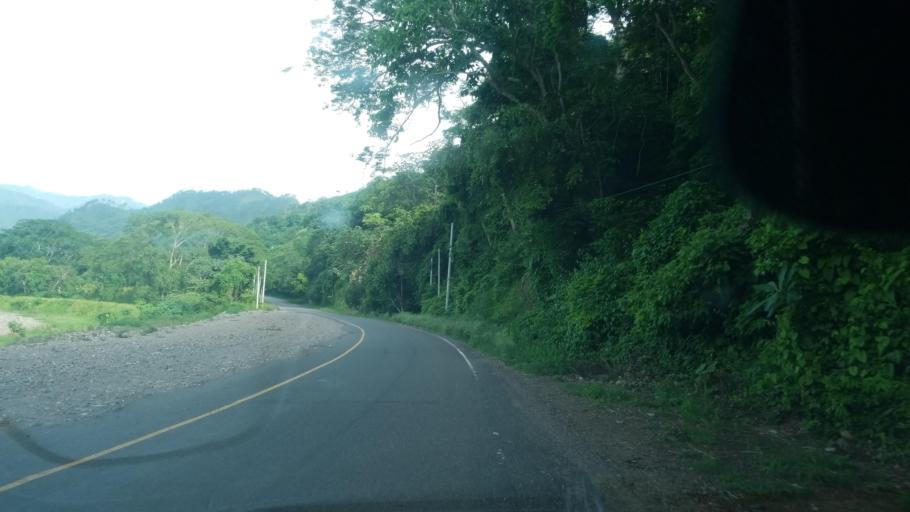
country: HN
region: Santa Barbara
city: Trinidad
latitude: 15.1256
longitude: -88.2092
